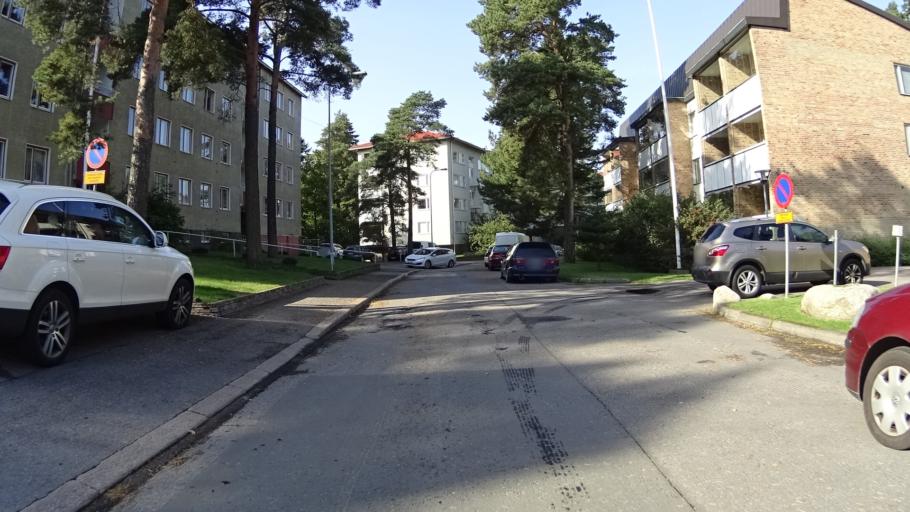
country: FI
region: Uusimaa
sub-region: Helsinki
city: Helsinki
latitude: 60.2094
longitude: 24.9030
